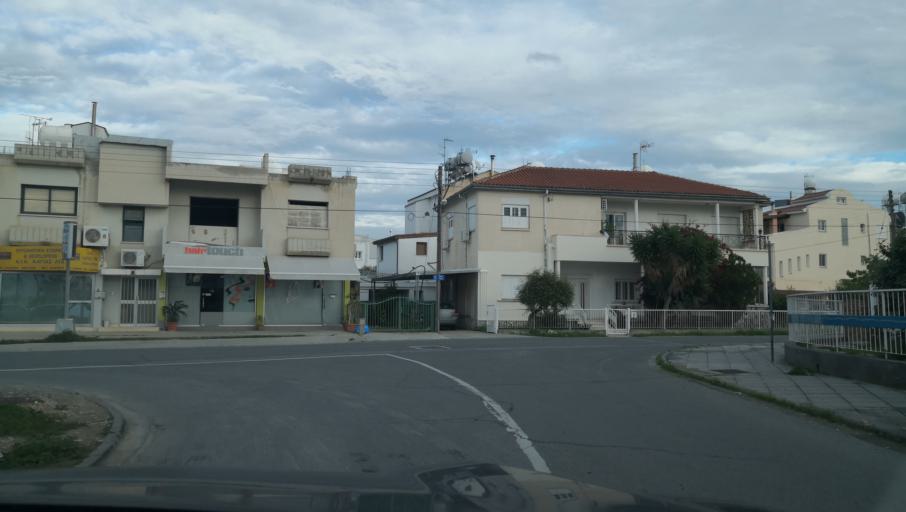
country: CY
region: Lefkosia
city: Nicosia
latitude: 35.1345
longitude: 33.3508
